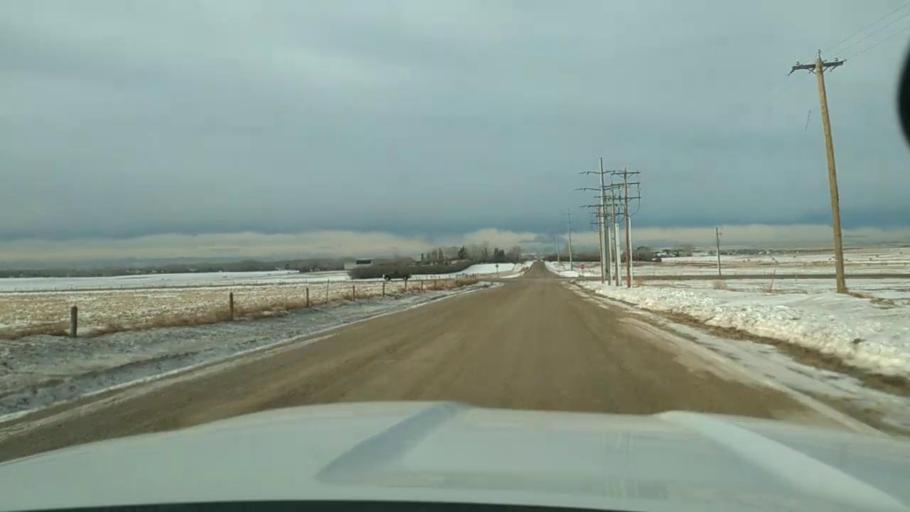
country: CA
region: Alberta
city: Airdrie
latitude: 51.2417
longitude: -113.9564
